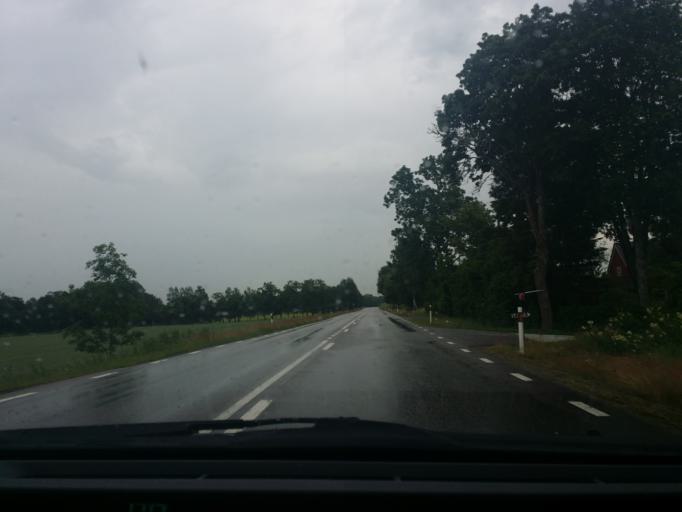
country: SE
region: OErebro
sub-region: Lindesbergs Kommun
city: Fellingsbro
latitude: 59.4657
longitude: 15.5557
